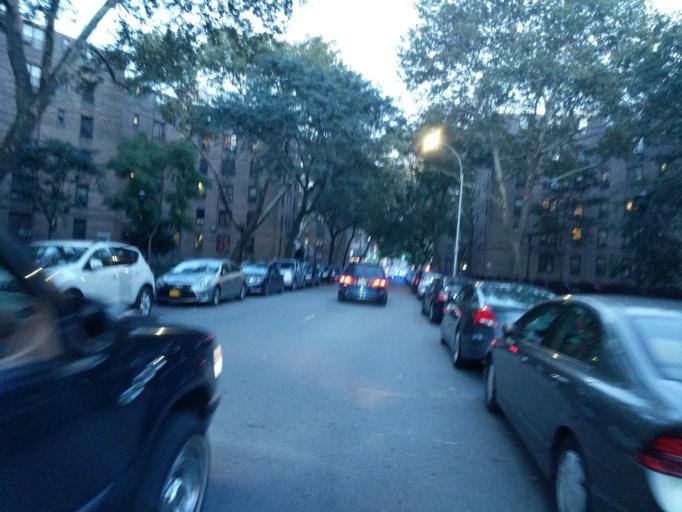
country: US
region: New York
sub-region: Queens County
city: Long Island City
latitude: 40.7546
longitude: -73.9436
